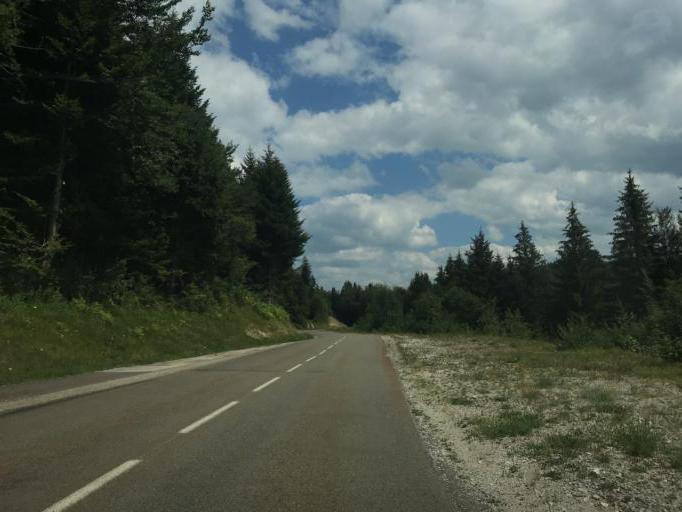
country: FR
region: Franche-Comte
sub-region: Departement du Jura
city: Clairvaux-les-Lacs
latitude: 46.5321
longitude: 5.7915
